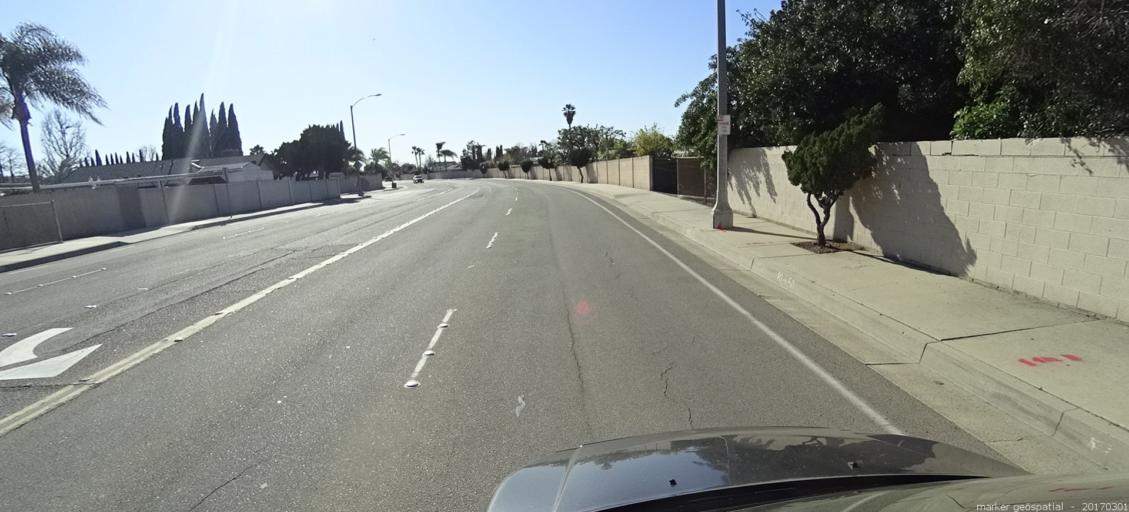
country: US
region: California
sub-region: Orange County
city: Villa Park
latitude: 33.8514
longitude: -117.8211
